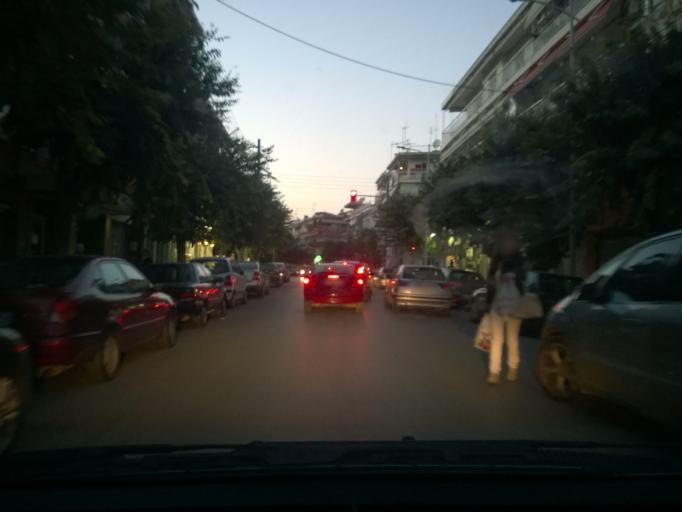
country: GR
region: Central Macedonia
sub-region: Nomos Thessalonikis
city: Ampelokipoi
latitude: 40.6489
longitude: 22.9268
